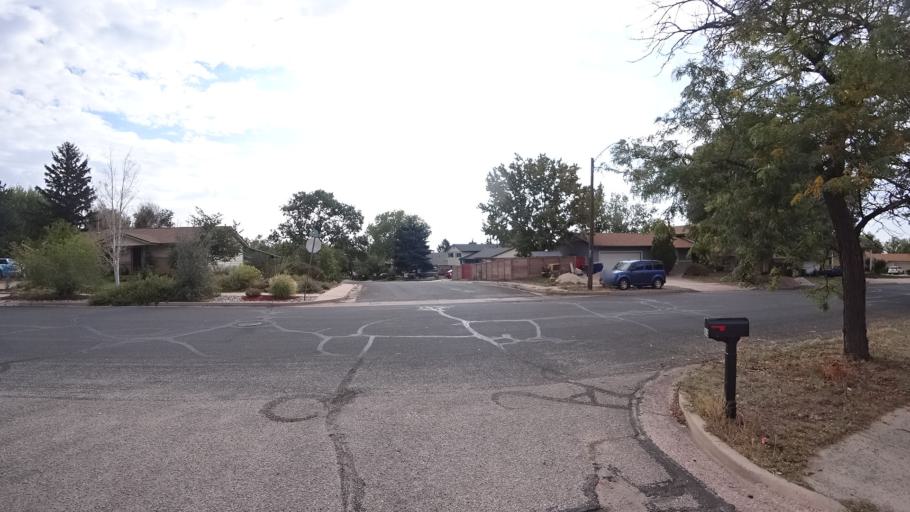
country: US
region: Colorado
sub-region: El Paso County
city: Cimarron Hills
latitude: 38.8426
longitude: -104.7507
